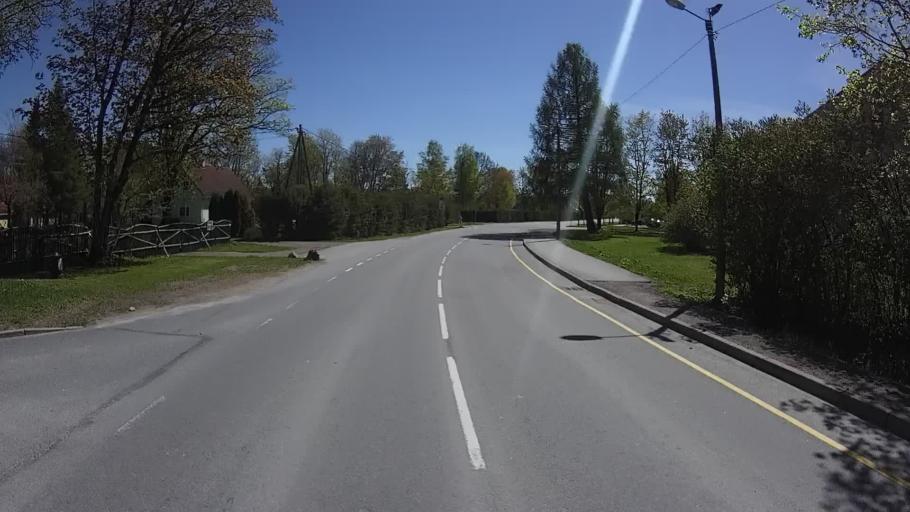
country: EE
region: Harju
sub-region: Raasiku vald
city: Raasiku
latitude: 59.1842
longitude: 25.1673
